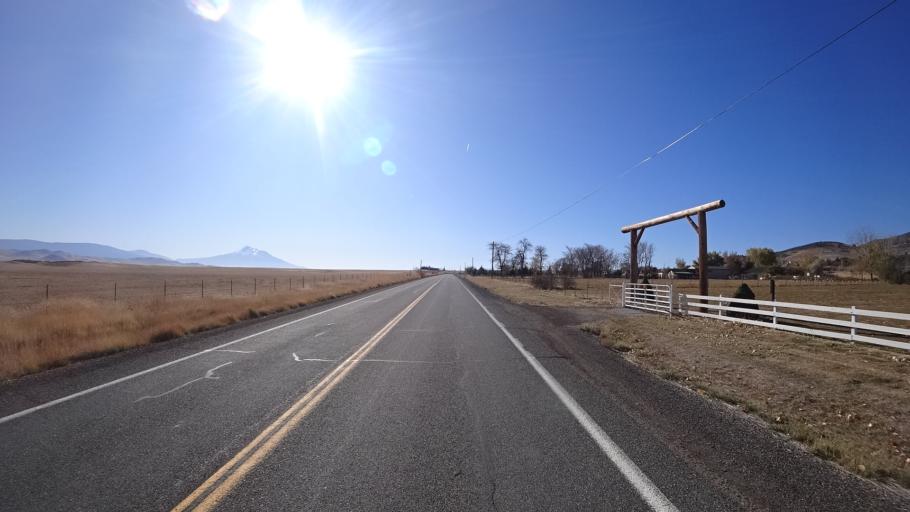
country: US
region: California
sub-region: Siskiyou County
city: Montague
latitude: 41.8130
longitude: -122.4984
